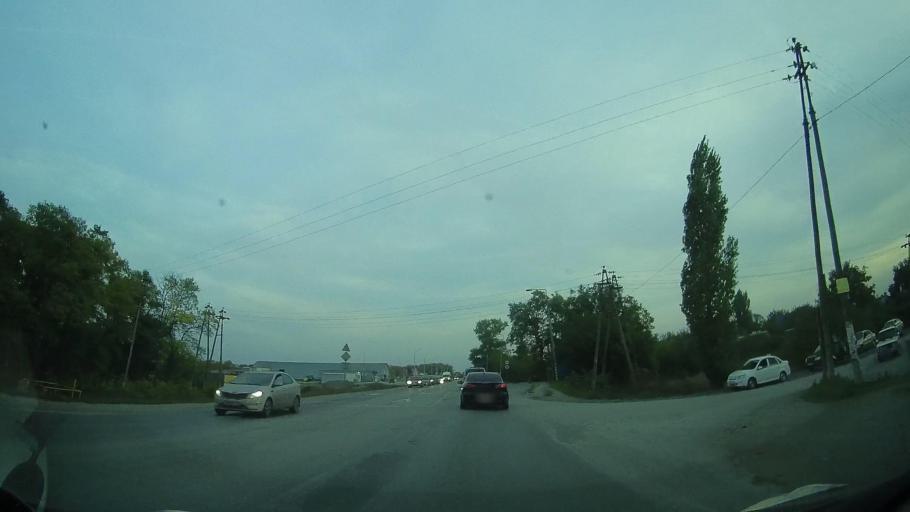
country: RU
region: Rostov
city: Kirovskaya
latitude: 46.9749
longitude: 40.0485
